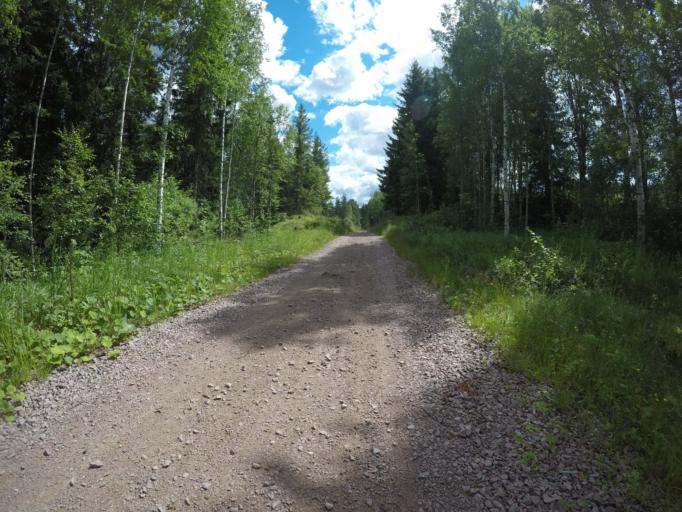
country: SE
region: Vaermland
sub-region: Filipstads Kommun
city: Lesjofors
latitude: 60.1248
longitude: 14.4313
